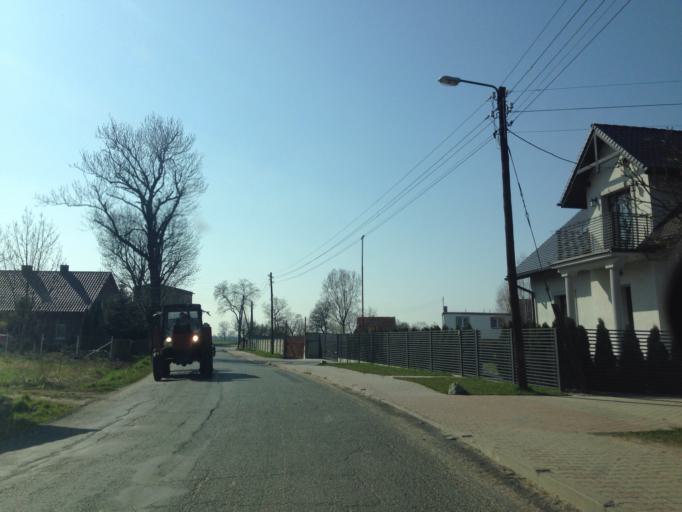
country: PL
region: Lower Silesian Voivodeship
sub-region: Powiat olesnicki
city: Bierutow
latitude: 51.1923
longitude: 17.4820
